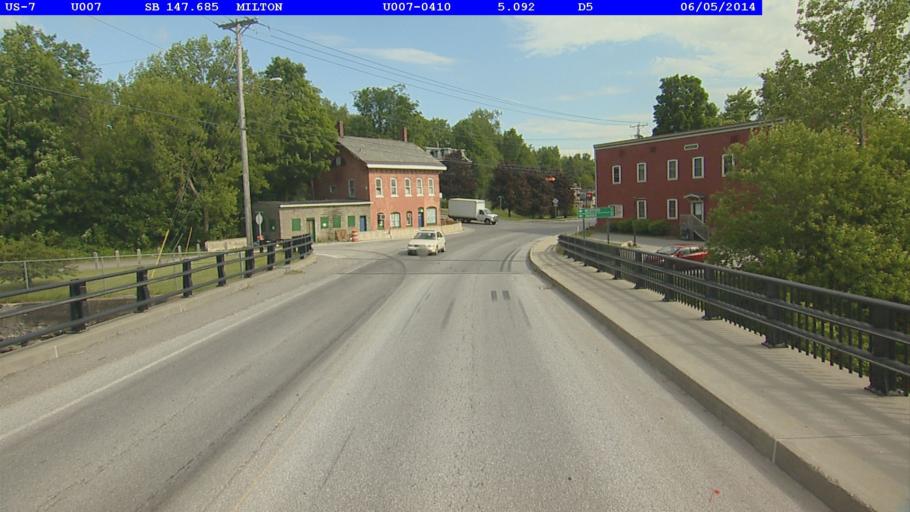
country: US
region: Vermont
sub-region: Chittenden County
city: Milton
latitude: 44.6406
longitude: -73.1137
